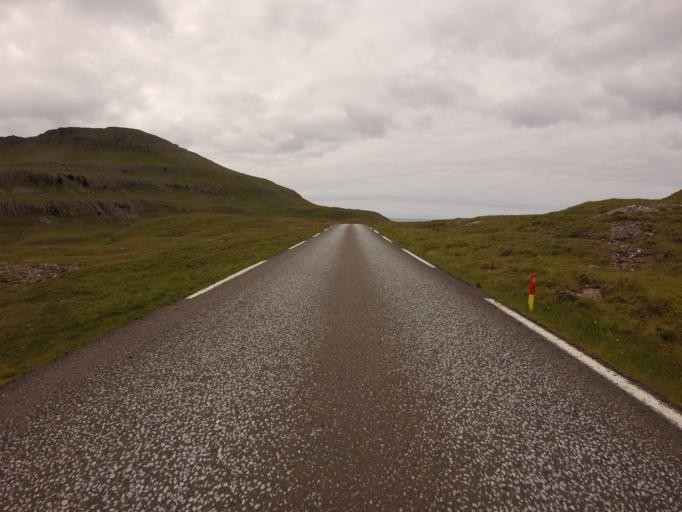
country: FO
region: Suduroy
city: Tvoroyri
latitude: 61.5181
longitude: -6.8631
